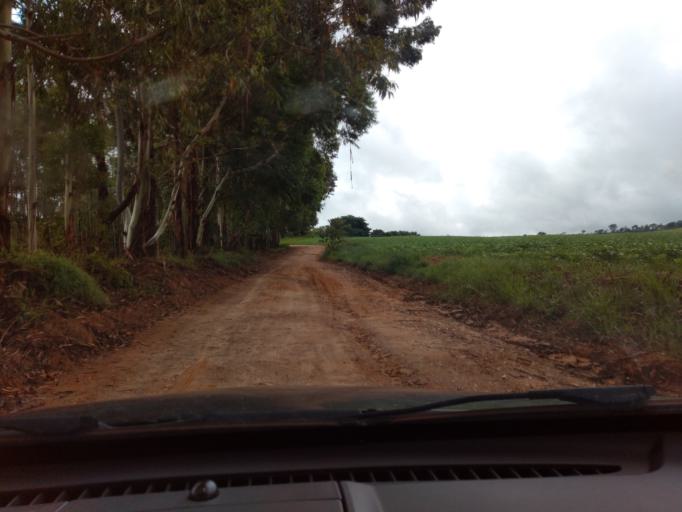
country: BR
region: Minas Gerais
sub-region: Lavras
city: Lavras
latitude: -21.5087
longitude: -44.9233
